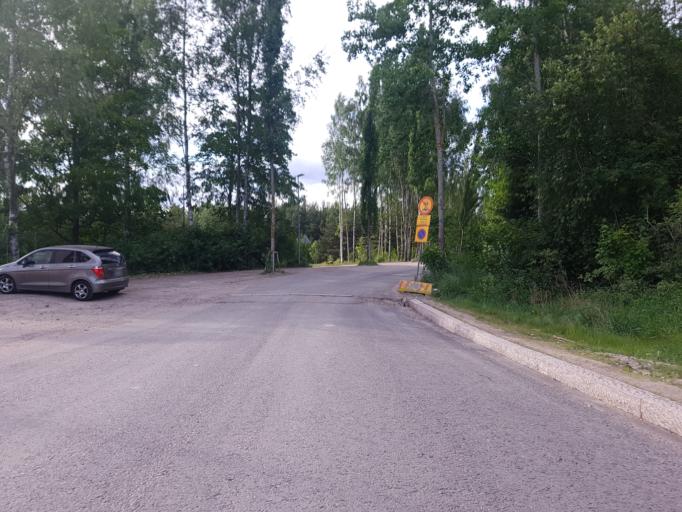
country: FI
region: Uusimaa
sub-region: Helsinki
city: Helsinki
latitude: 60.2344
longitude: 24.9483
